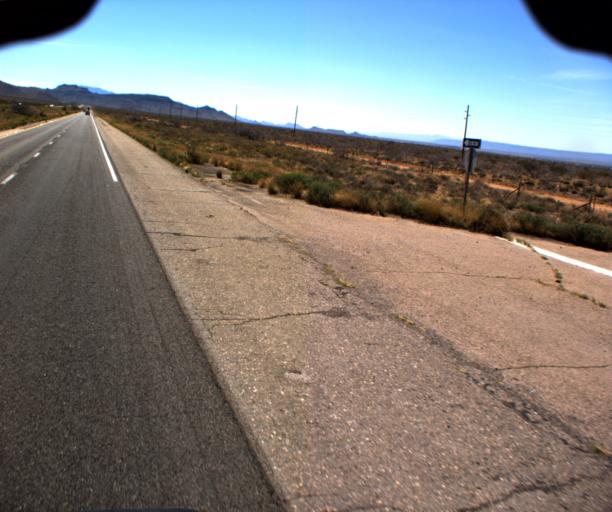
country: US
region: Arizona
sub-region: Mohave County
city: Golden Valley
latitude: 35.2810
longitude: -114.1757
